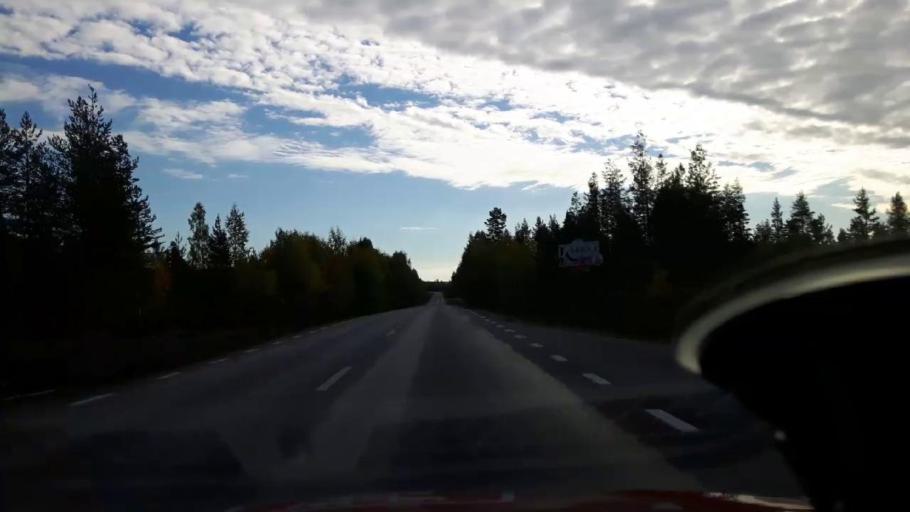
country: SE
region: Gaevleborg
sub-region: Ljusdals Kommun
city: Farila
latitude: 61.9902
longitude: 15.2696
